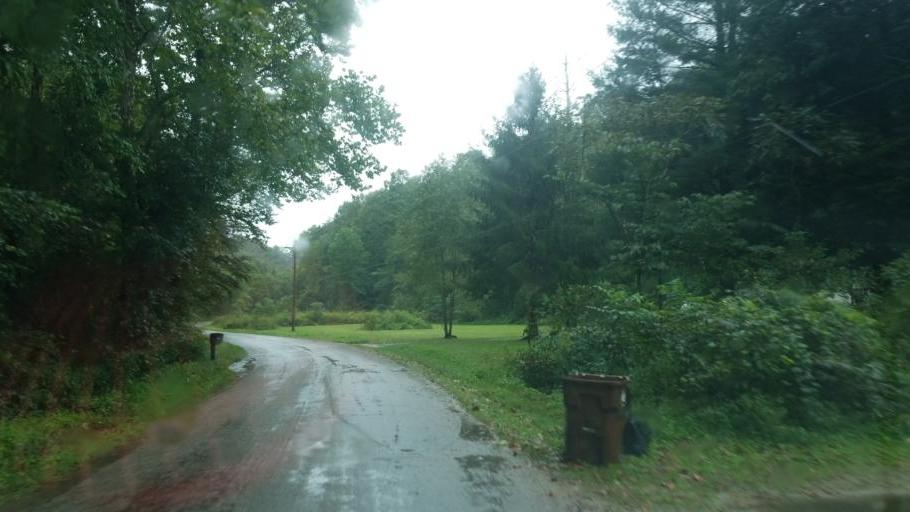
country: US
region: Ohio
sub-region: Adams County
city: Peebles
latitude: 38.8051
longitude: -83.2493
